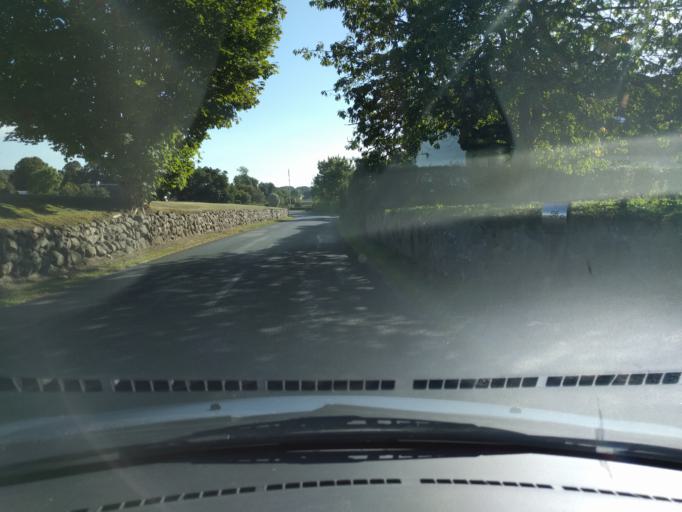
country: DK
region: South Denmark
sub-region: Assens Kommune
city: Harby
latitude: 55.1507
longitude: 10.0181
